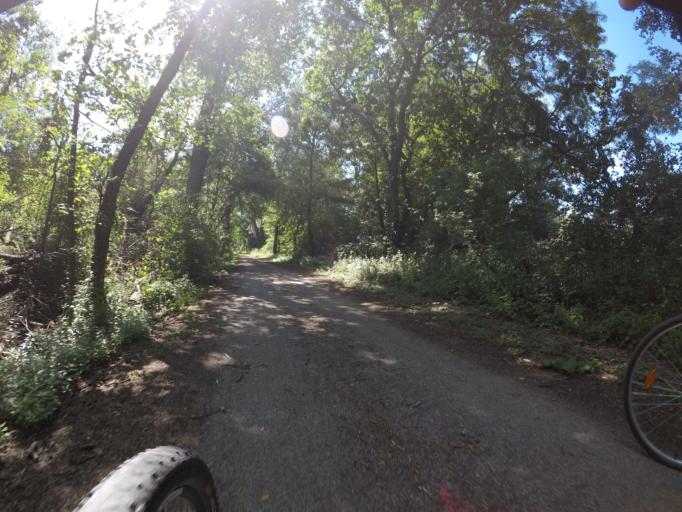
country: AT
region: Lower Austria
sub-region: Politischer Bezirk Ganserndorf
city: Gross-Enzersdorf
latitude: 48.1812
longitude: 16.5198
